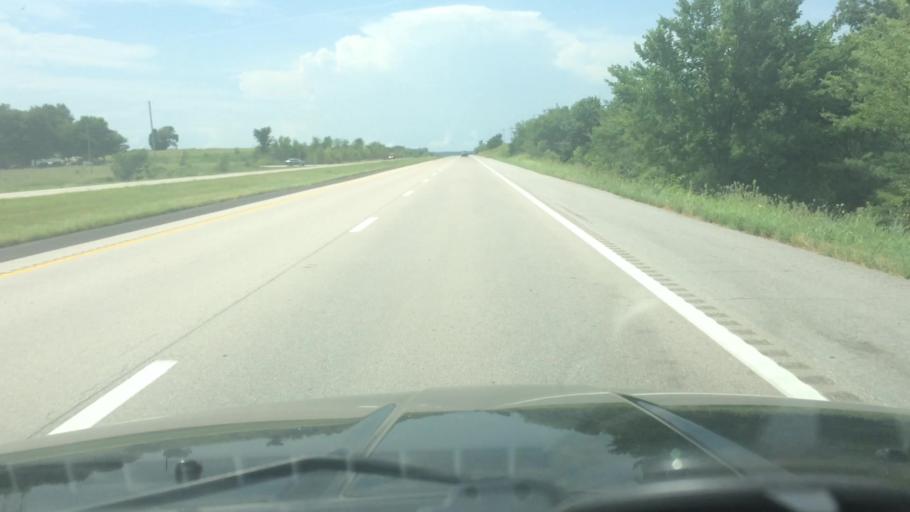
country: US
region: Missouri
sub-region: Polk County
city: Humansville
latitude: 37.7985
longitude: -93.5926
